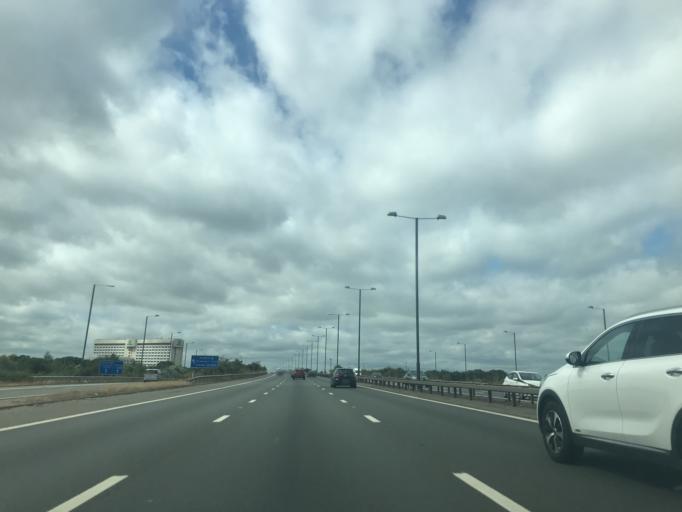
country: GB
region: England
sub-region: Greater London
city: West Drayton
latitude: 51.4954
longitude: -0.4464
